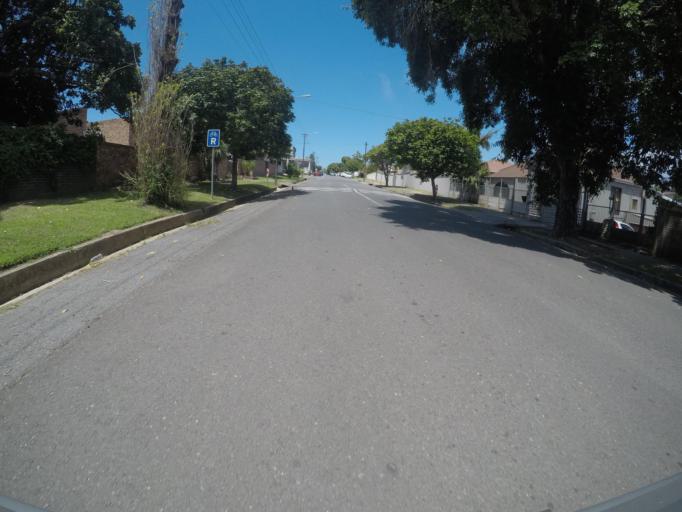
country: ZA
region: Eastern Cape
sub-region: Buffalo City Metropolitan Municipality
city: East London
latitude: -32.9896
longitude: 27.9055
